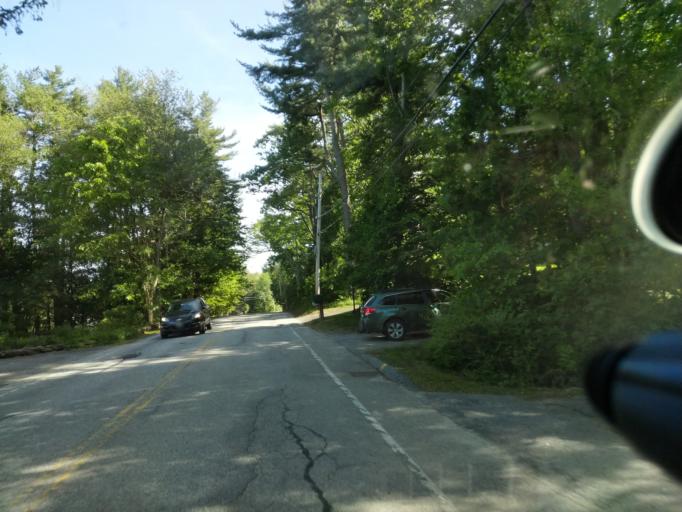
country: US
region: Maine
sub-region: Cumberland County
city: Falmouth
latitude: 43.7346
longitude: -70.3061
